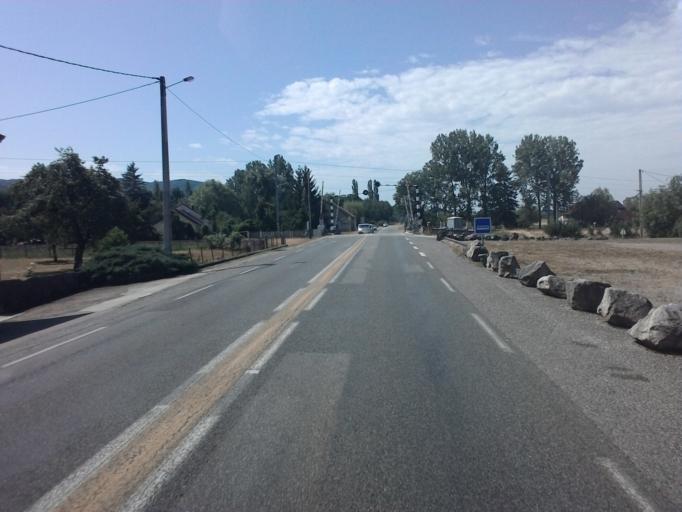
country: FR
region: Franche-Comte
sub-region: Departement du Jura
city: Cousance
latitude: 46.5987
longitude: 5.4596
